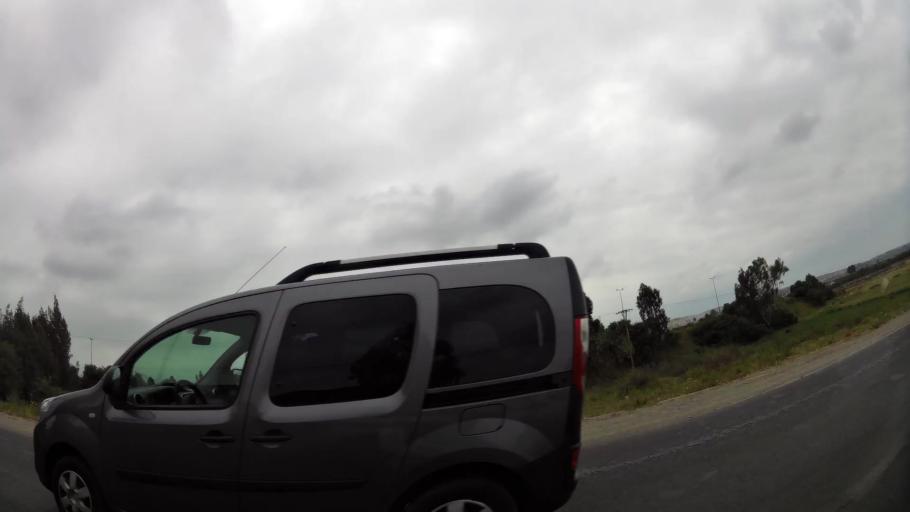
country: MA
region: Rabat-Sale-Zemmour-Zaer
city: Sale
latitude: 33.9887
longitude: -6.7629
